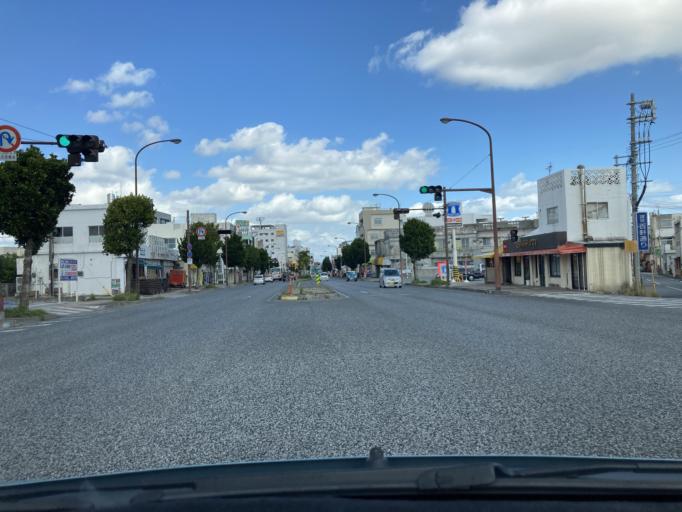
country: JP
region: Okinawa
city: Okinawa
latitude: 26.3262
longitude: 127.7933
